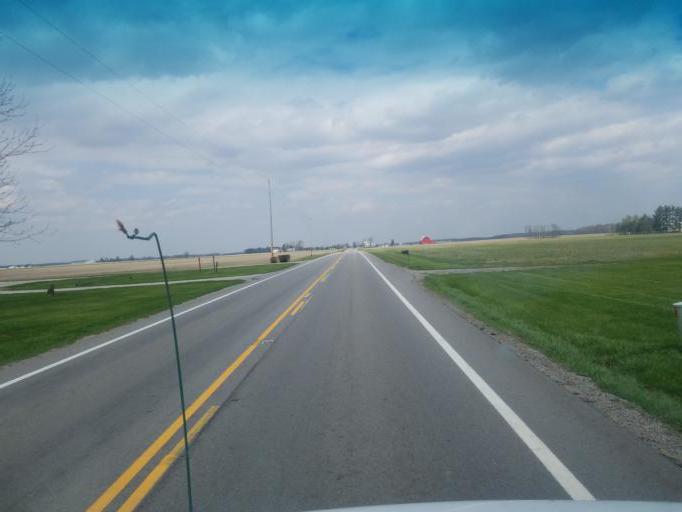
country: US
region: Ohio
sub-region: Wyandot County
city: Upper Sandusky
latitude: 40.9018
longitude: -83.2752
